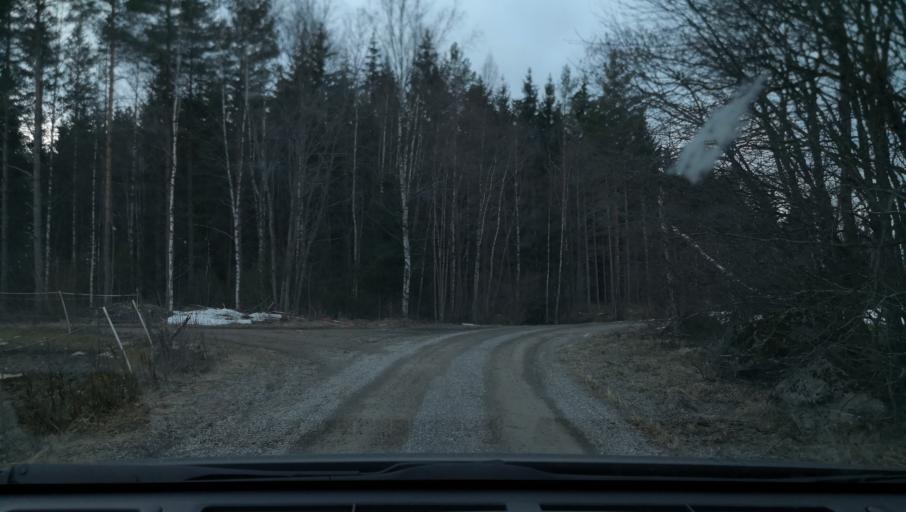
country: SE
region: Vaestmanland
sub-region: Kopings Kommun
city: Kolsva
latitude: 59.5608
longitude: 15.8386
